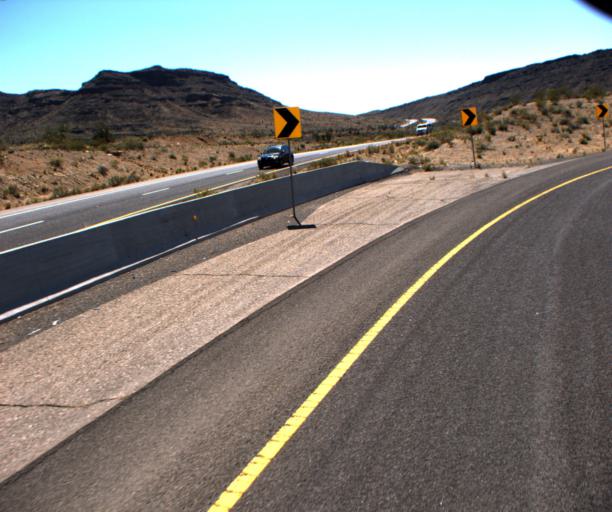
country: US
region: Arizona
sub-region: Mohave County
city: Kingman
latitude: 35.2212
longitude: -114.1219
